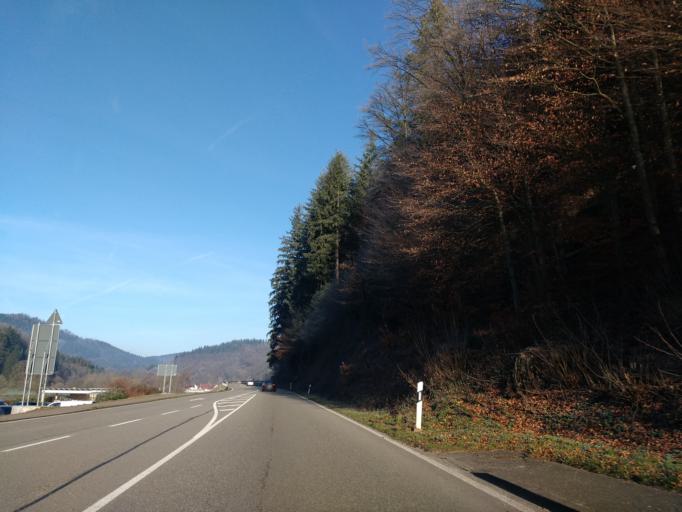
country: DE
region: Baden-Wuerttemberg
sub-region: Freiburg Region
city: Oppenau
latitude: 48.4795
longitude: 8.1535
